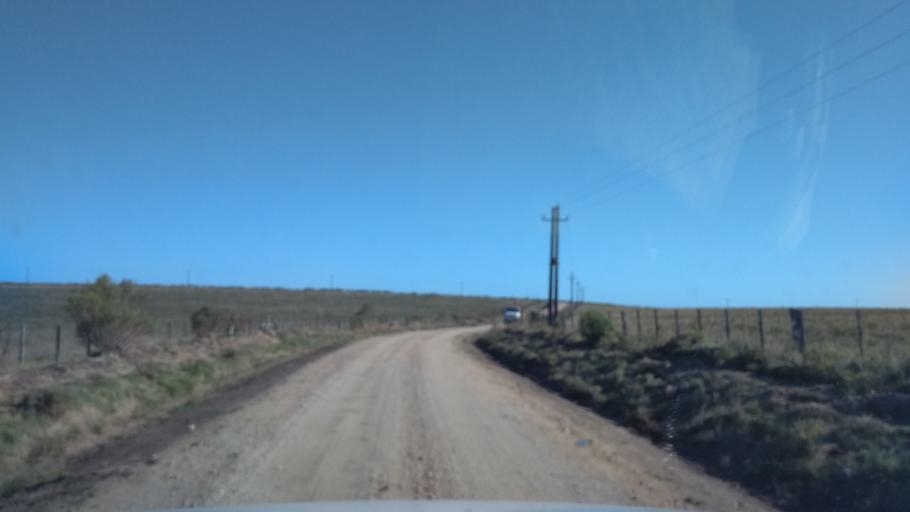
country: UY
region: Florida
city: Casupa
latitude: -34.0041
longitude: -55.7877
